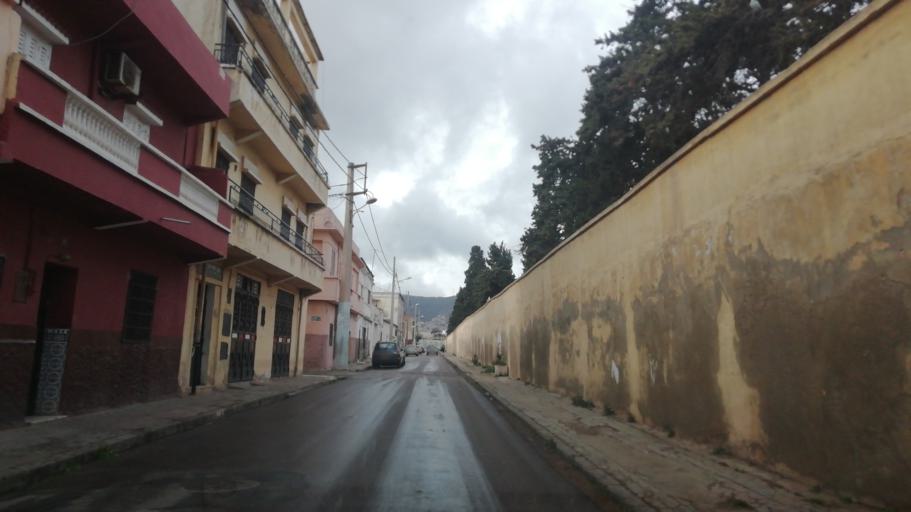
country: DZ
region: Oran
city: Oran
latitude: 35.6904
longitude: -0.6381
